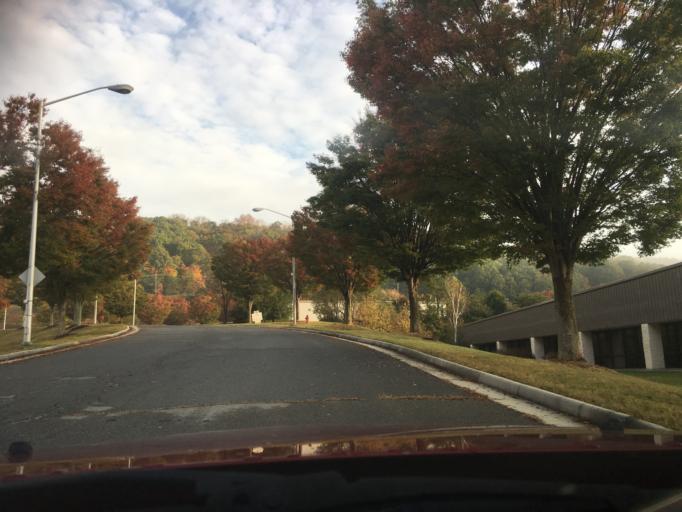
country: US
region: Virginia
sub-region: City of Radford
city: Radford
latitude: 37.0950
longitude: -80.5750
